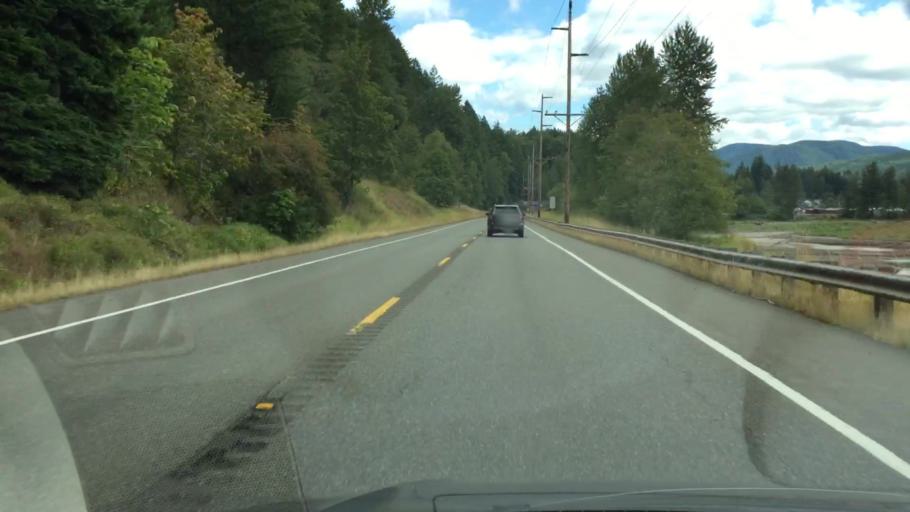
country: US
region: Washington
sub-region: Pierce County
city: Eatonville
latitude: 46.7693
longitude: -122.2033
